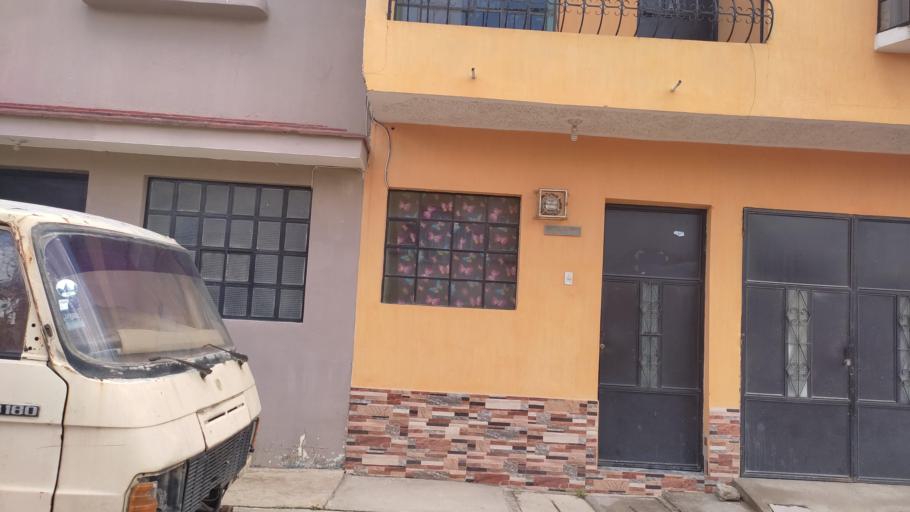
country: GT
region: Quetzaltenango
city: Olintepeque
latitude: 14.8618
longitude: -91.5241
